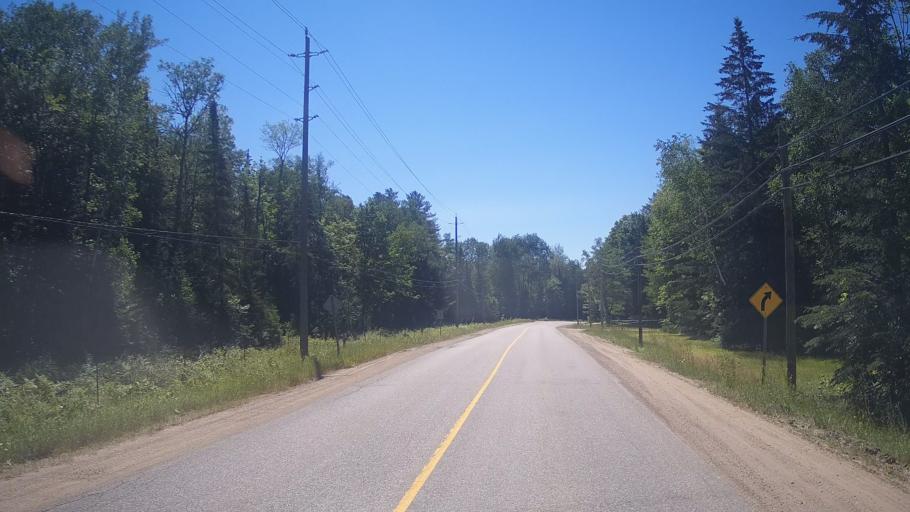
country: CA
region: Ontario
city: Huntsville
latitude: 45.3718
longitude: -79.2083
